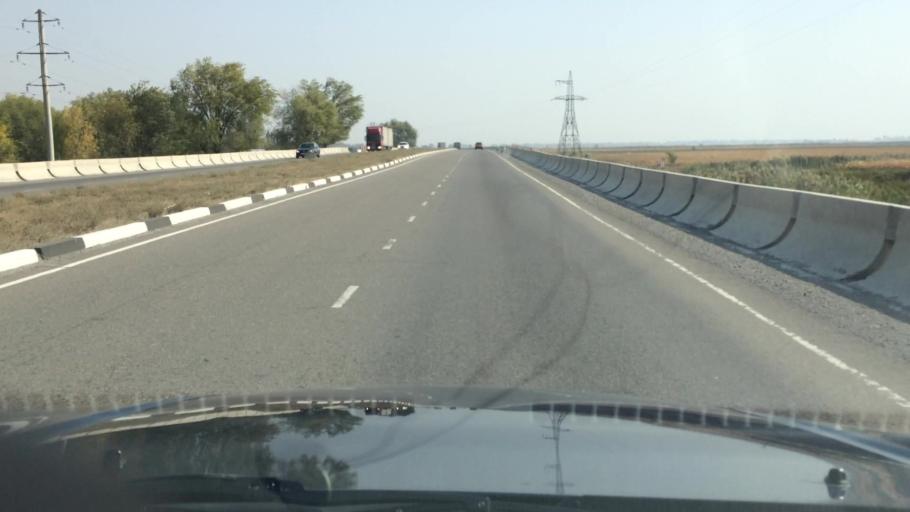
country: KG
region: Chuy
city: Kant
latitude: 42.9672
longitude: 74.8350
